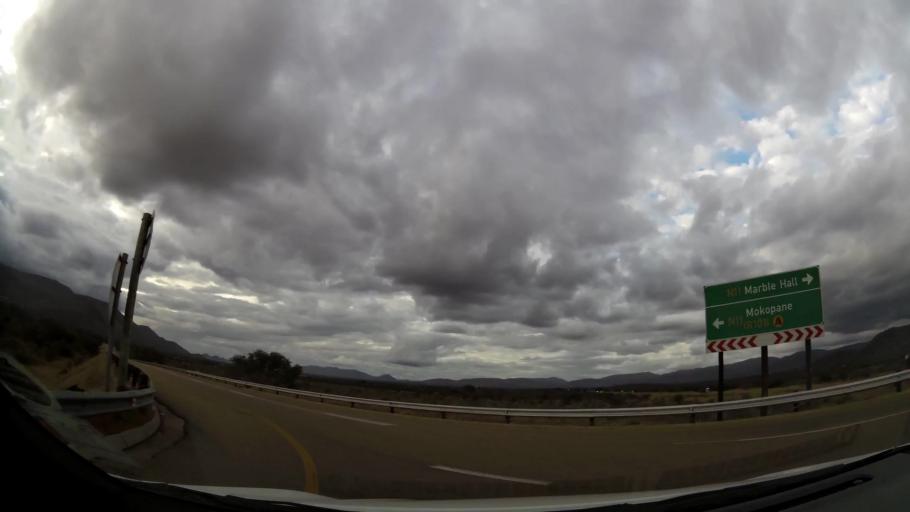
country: ZA
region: Limpopo
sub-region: Waterberg District Municipality
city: Mokopane
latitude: -24.2858
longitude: 28.9815
